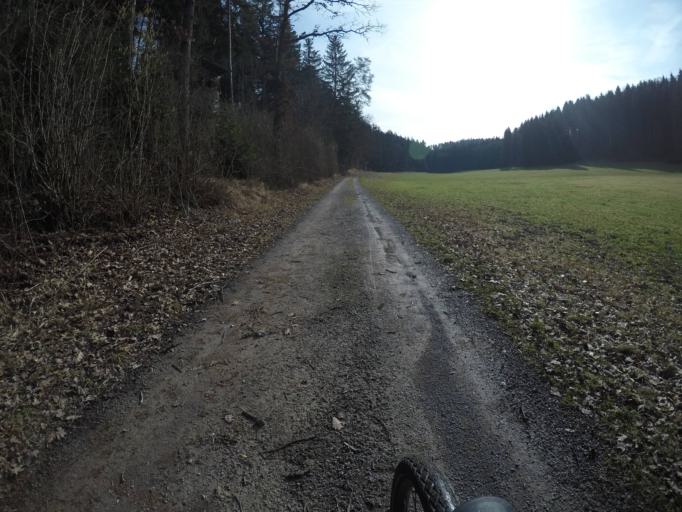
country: DE
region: Baden-Wuerttemberg
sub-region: Regierungsbezirk Stuttgart
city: Oberjettingen
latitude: 48.6003
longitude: 8.7891
